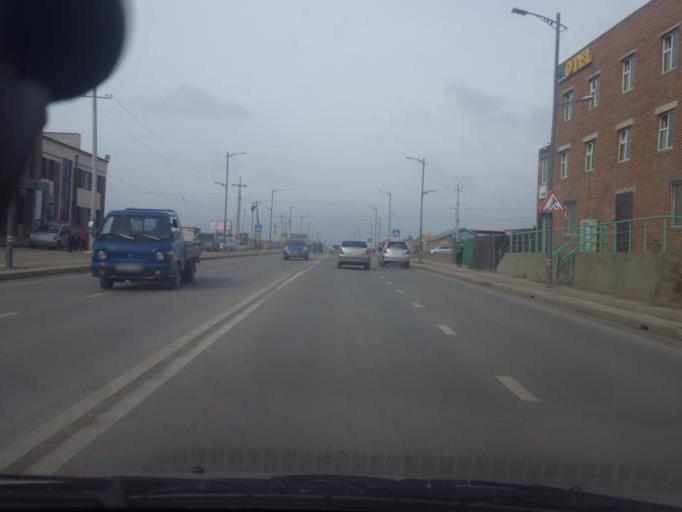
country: MN
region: Ulaanbaatar
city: Ulaanbaatar
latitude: 47.9204
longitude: 106.8013
